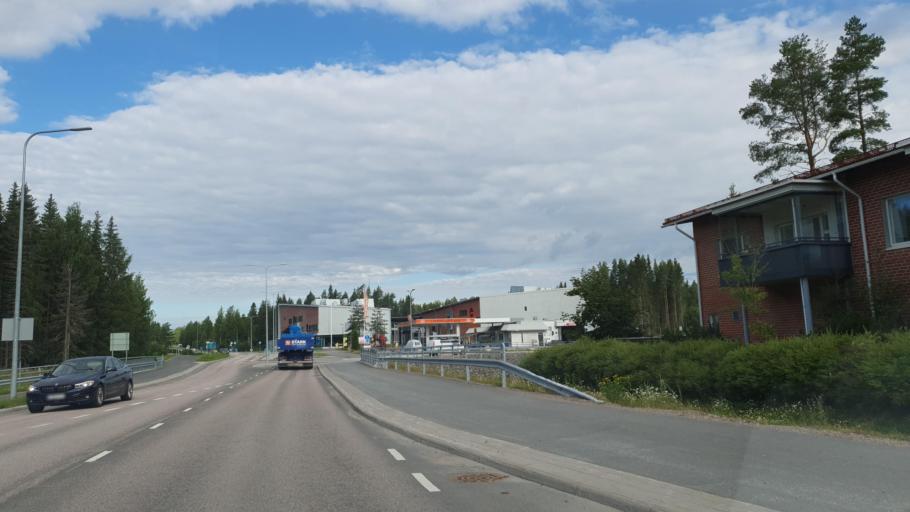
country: FI
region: Central Finland
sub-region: Jyvaeskylae
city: Jyvaeskylae
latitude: 62.1891
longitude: 25.7119
